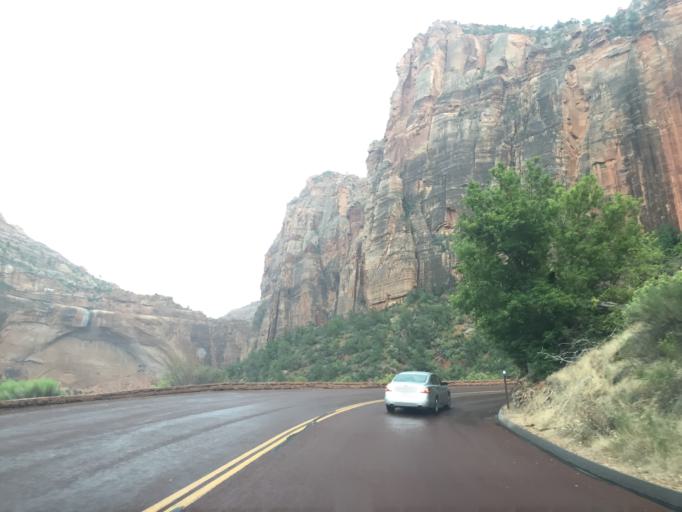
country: US
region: Utah
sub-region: Washington County
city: Hildale
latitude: 37.2124
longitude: -112.9565
